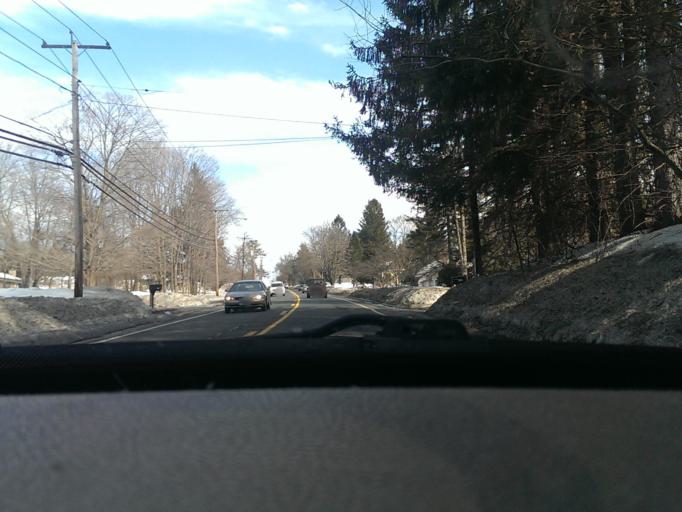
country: US
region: Massachusetts
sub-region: Hampden County
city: Wilbraham
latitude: 42.1525
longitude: -72.4043
